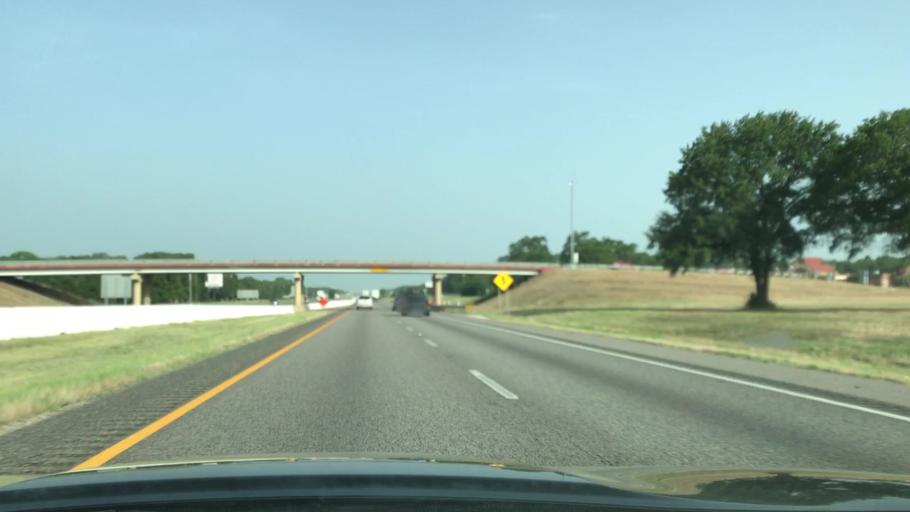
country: US
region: Texas
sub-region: Van Zandt County
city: Canton
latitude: 32.5855
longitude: -95.8721
